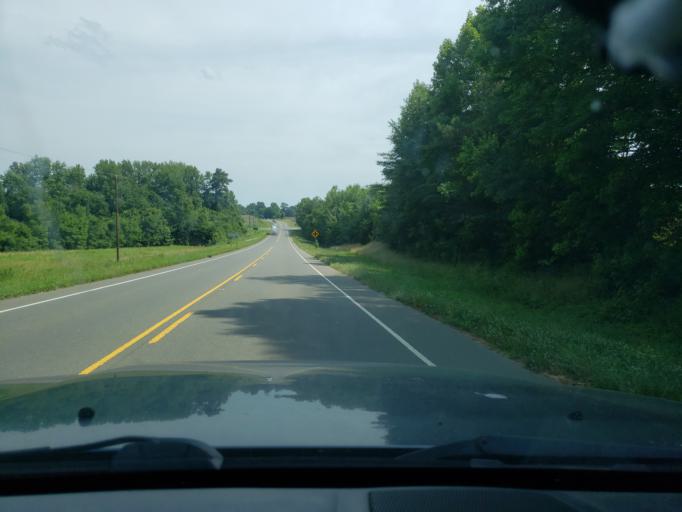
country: US
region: North Carolina
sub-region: Alamance County
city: Saxapahaw
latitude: 35.9782
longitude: -79.2806
